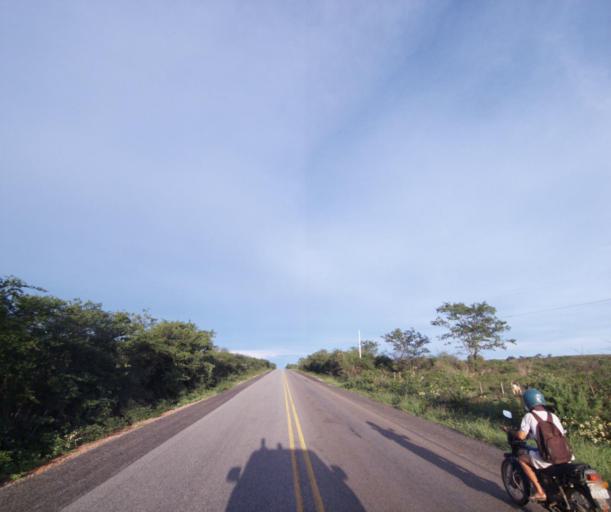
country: BR
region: Bahia
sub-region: Cacule
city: Cacule
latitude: -14.2102
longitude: -42.0925
